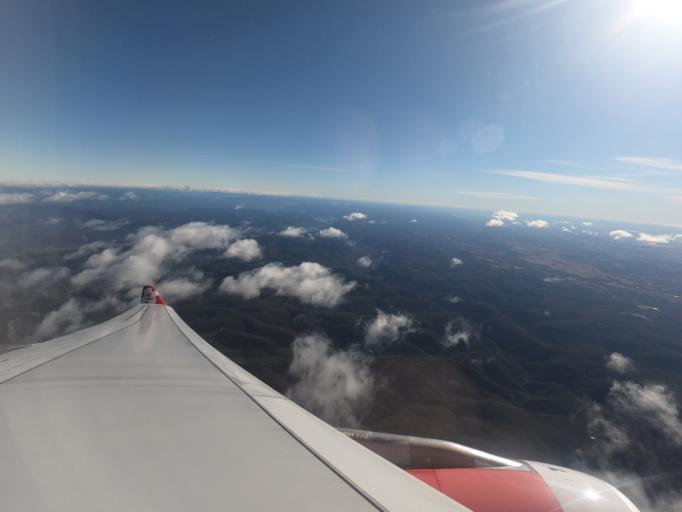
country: AU
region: New South Wales
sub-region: Wollondilly
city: Buxton
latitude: -34.2705
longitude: 150.4388
